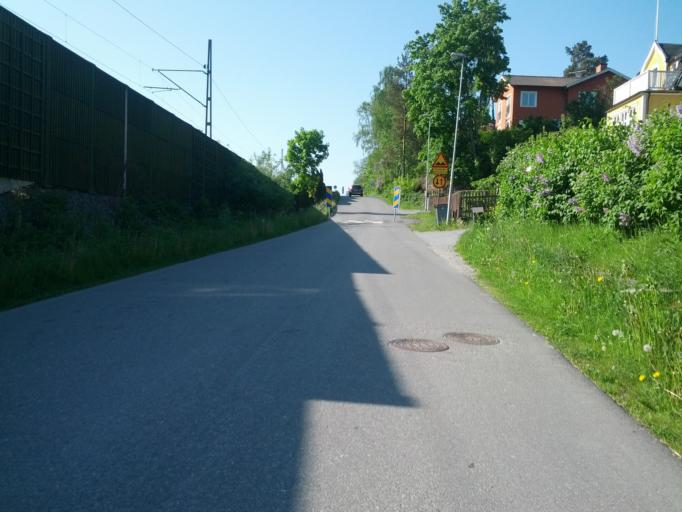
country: SE
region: Stockholm
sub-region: Taby Kommun
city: Taby
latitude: 59.4299
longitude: 18.0509
